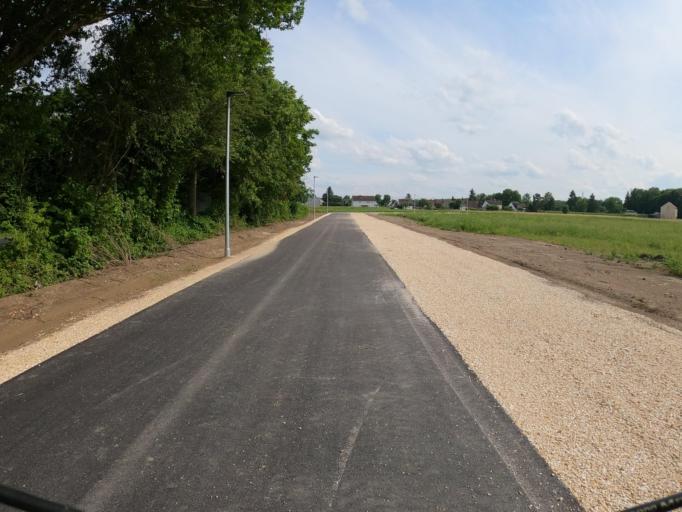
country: DE
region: Bavaria
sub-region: Swabia
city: Neu-Ulm
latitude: 48.3737
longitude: 10.0036
